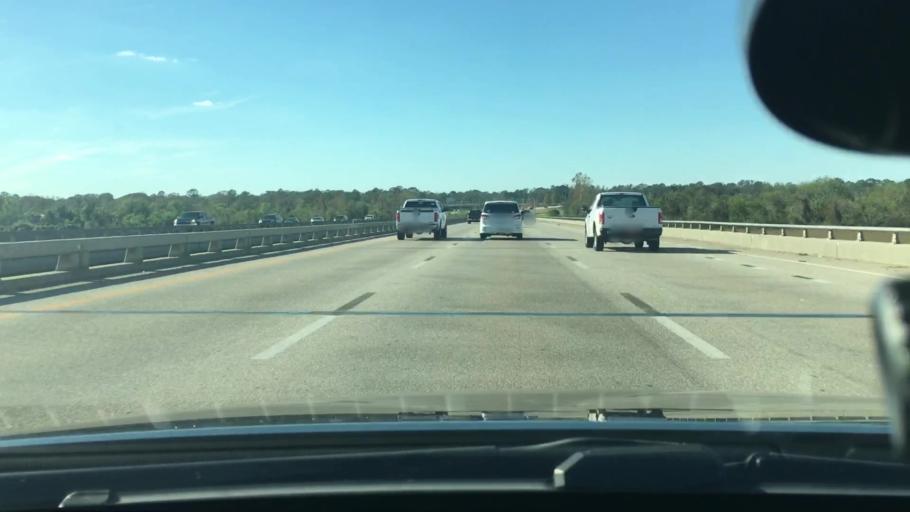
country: US
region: North Carolina
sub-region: Craven County
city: New Bern
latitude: 35.0977
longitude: -77.0490
